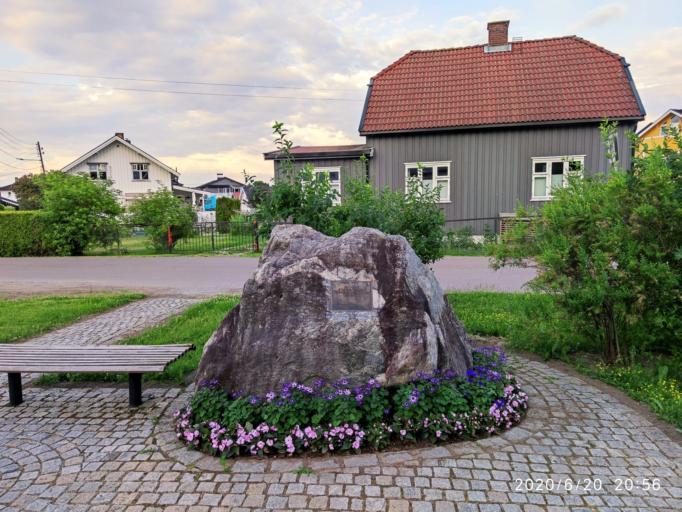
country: NO
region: Akershus
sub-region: Skedsmo
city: Lillestrom
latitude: 59.9550
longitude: 11.0574
